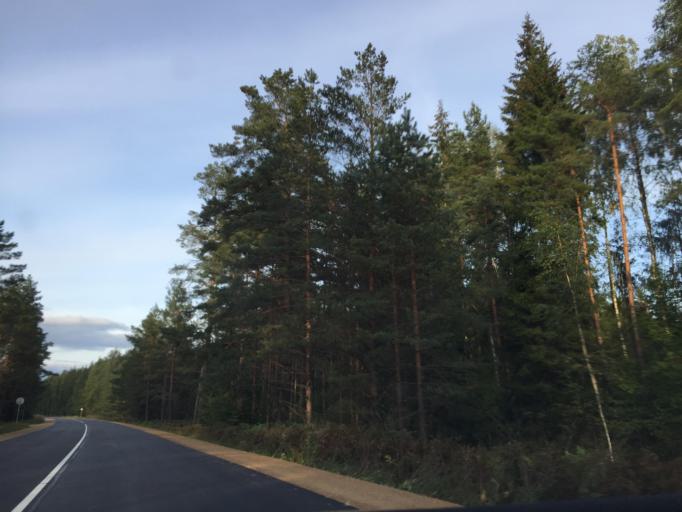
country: LV
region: Viesite
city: Viesite
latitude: 56.3752
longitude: 25.6577
